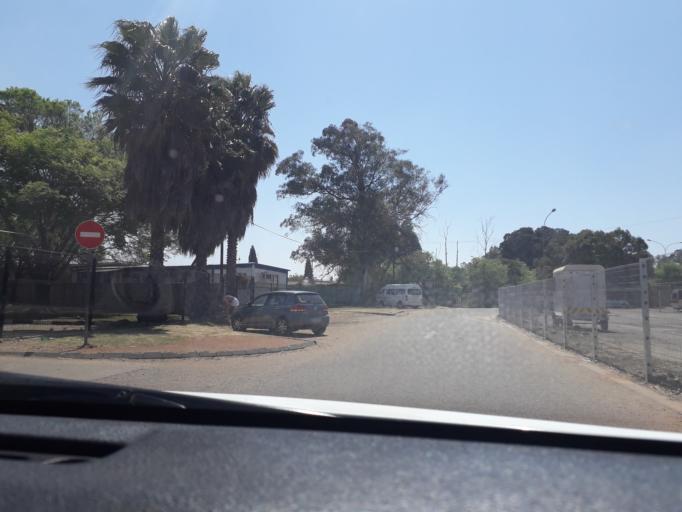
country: ZA
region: Gauteng
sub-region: City of Johannesburg Metropolitan Municipality
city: Modderfontein
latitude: -26.1091
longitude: 28.2263
